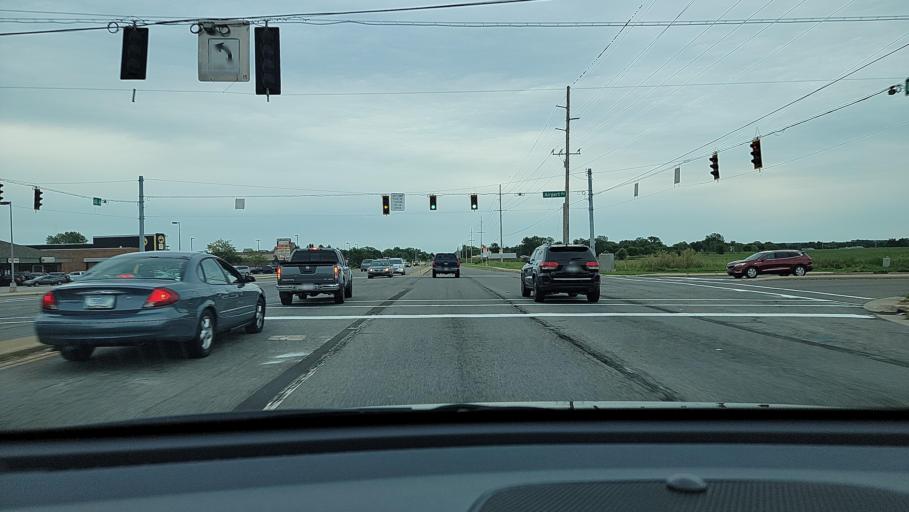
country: US
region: Indiana
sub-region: Porter County
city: South Haven
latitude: 41.5505
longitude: -87.1637
